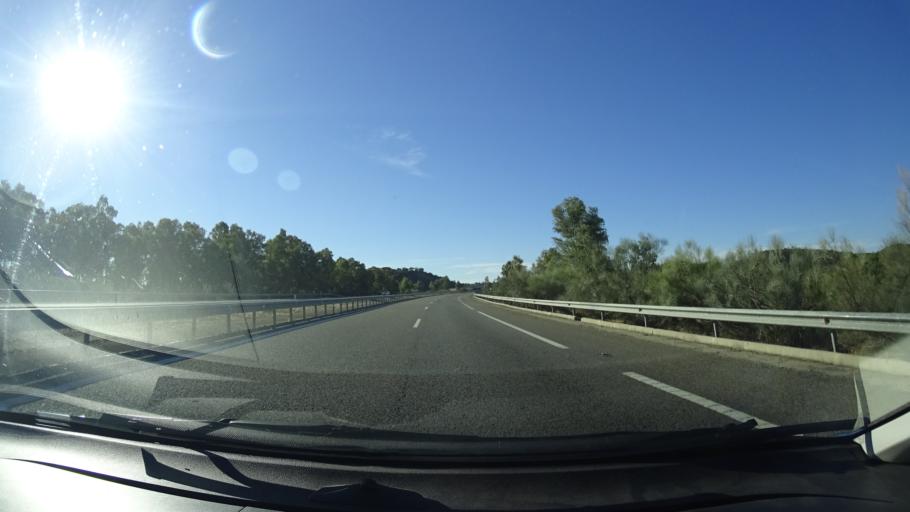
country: ES
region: Andalusia
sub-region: Provincia de Sevilla
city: El Ronquillo
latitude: 37.8091
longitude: -6.2033
